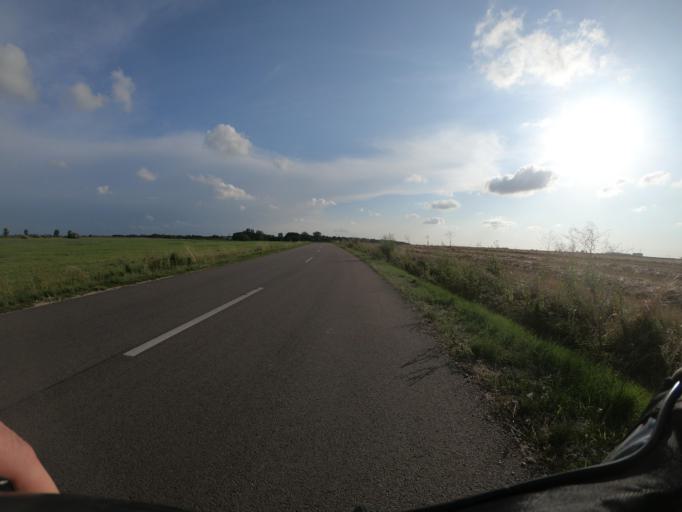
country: HU
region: Borsod-Abauj-Zemplen
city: Mezokeresztes
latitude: 47.8184
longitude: 20.7446
